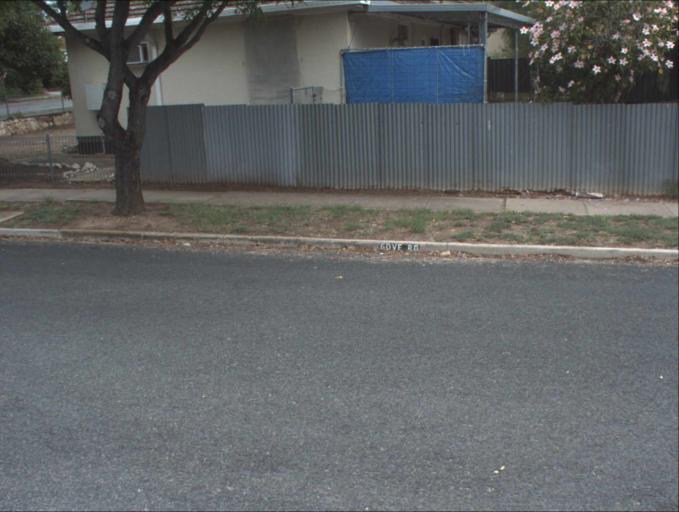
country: AU
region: South Australia
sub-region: Port Adelaide Enfield
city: Enfield
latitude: -34.8561
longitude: 138.6051
